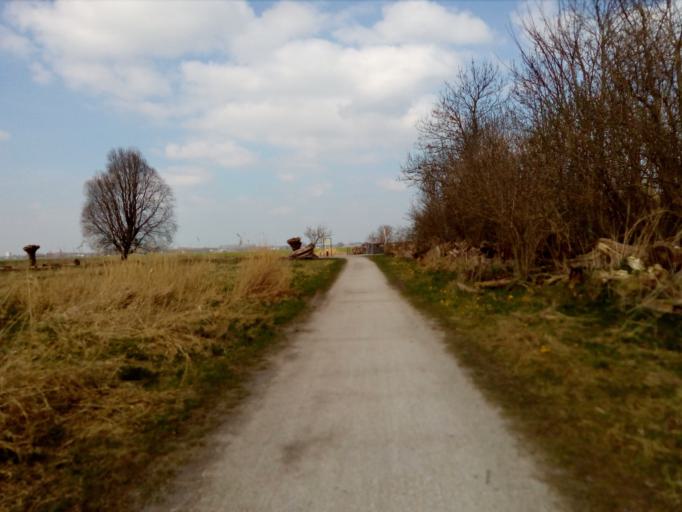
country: NL
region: South Holland
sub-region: Gemeente Zoetermeer
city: Zoetermeer
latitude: 52.0765
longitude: 4.4558
